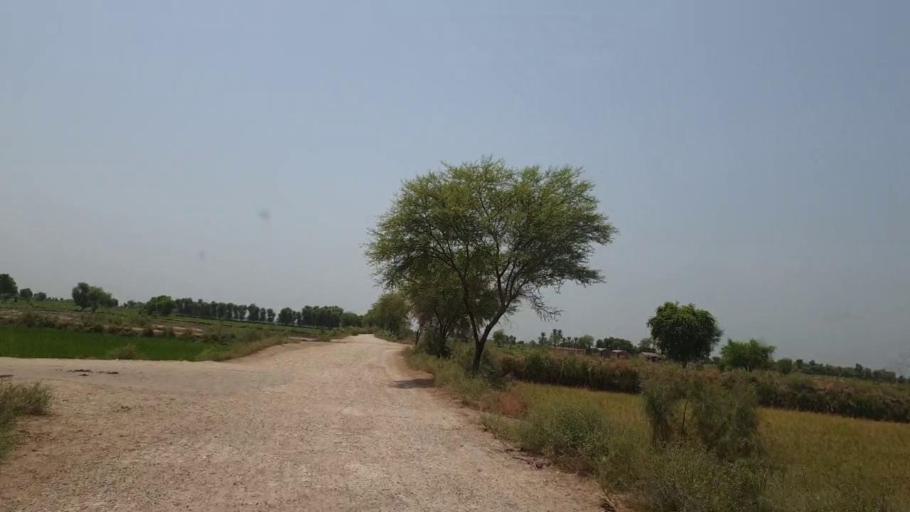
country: PK
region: Sindh
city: Shikarpur
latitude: 27.8881
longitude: 68.6299
